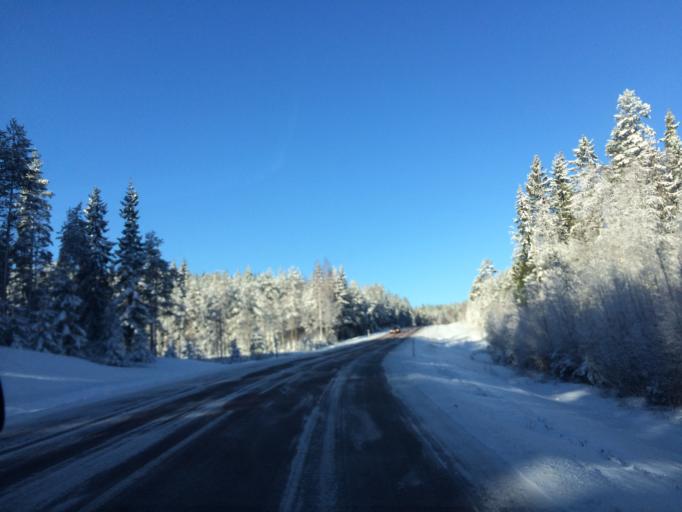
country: SE
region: Dalarna
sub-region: Mora Kommun
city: Mora
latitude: 60.8533
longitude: 14.3182
